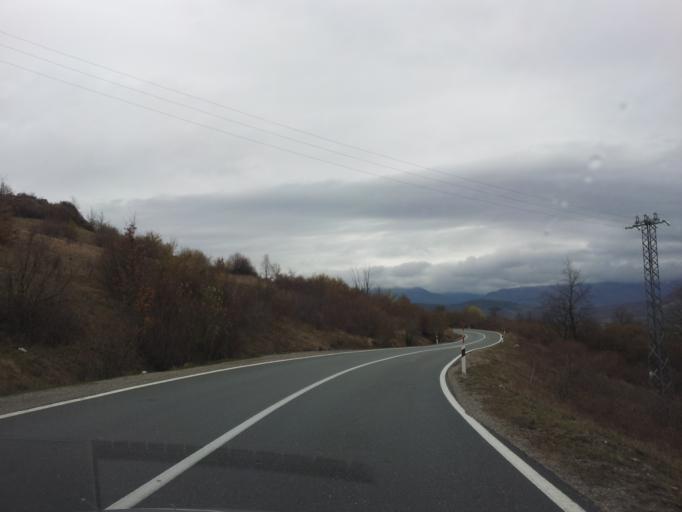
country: HR
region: Zadarska
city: Gracac
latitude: 44.4920
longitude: 15.7432
